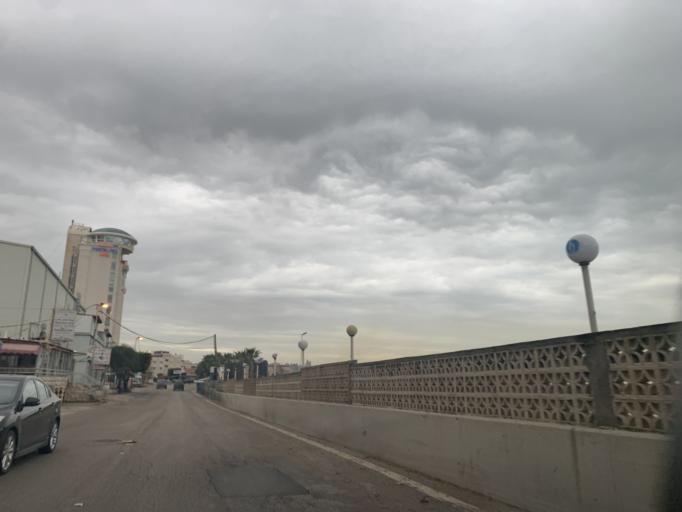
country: LB
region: Mont-Liban
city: Djounie
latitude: 33.9964
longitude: 35.6426
